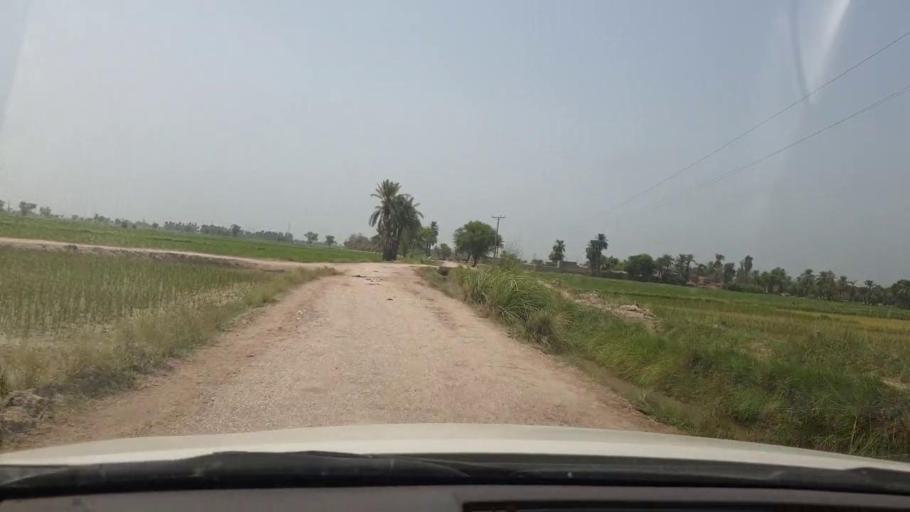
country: PK
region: Sindh
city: Shikarpur
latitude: 28.0104
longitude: 68.6475
